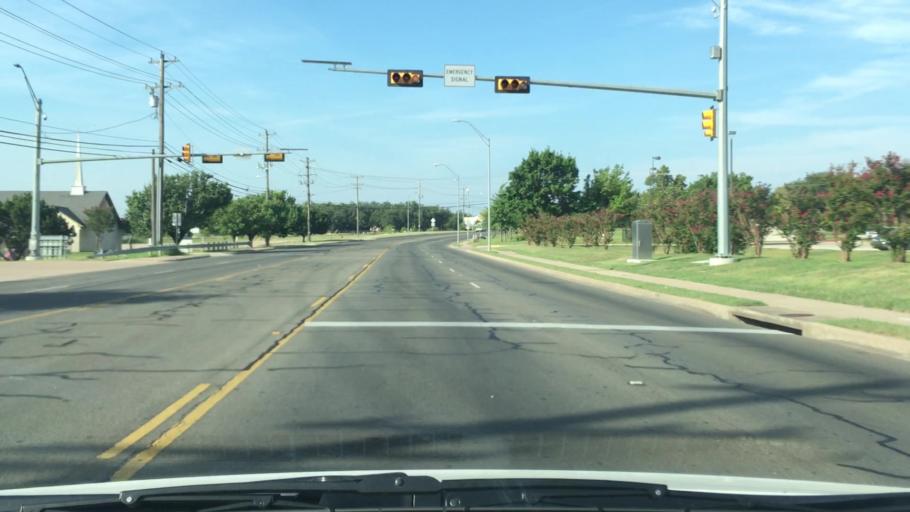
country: US
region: Texas
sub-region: Williamson County
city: Cedar Park
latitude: 30.4791
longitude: -97.8338
